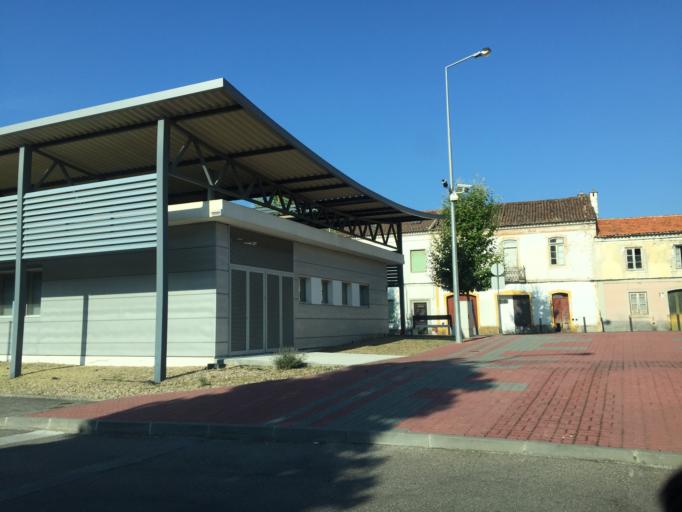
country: PT
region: Santarem
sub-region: Abrantes
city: Abrantes
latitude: 39.4748
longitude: -8.1886
